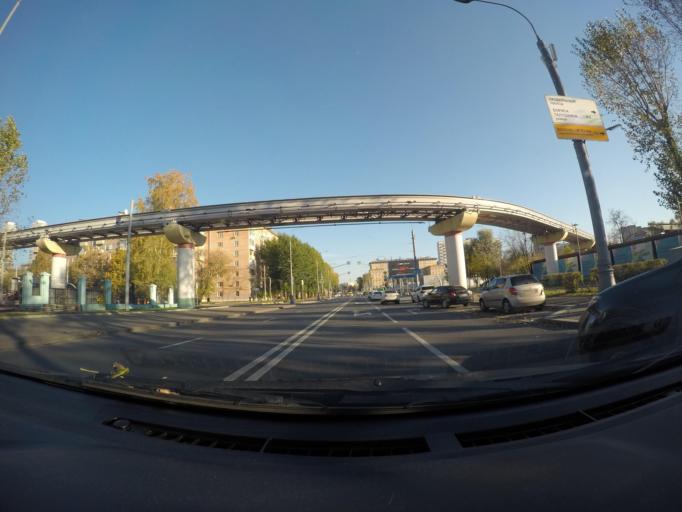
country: RU
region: Moscow
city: Leonovo
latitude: 55.8306
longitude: 37.6450
